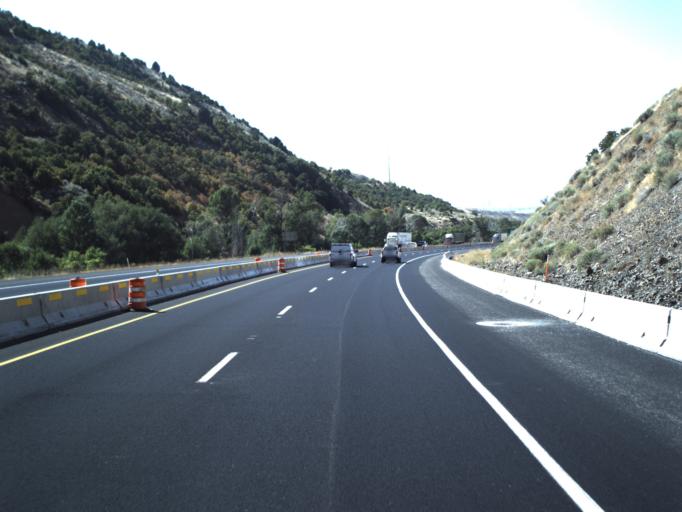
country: US
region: Utah
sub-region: Box Elder County
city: Brigham City
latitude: 41.4979
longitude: -111.9754
